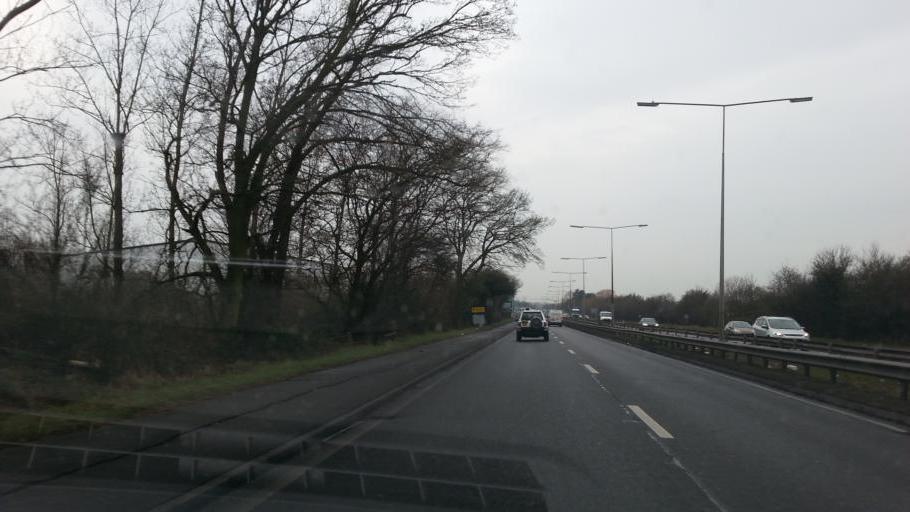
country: GB
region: England
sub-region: Essex
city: Wickford
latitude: 51.5914
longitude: 0.5122
